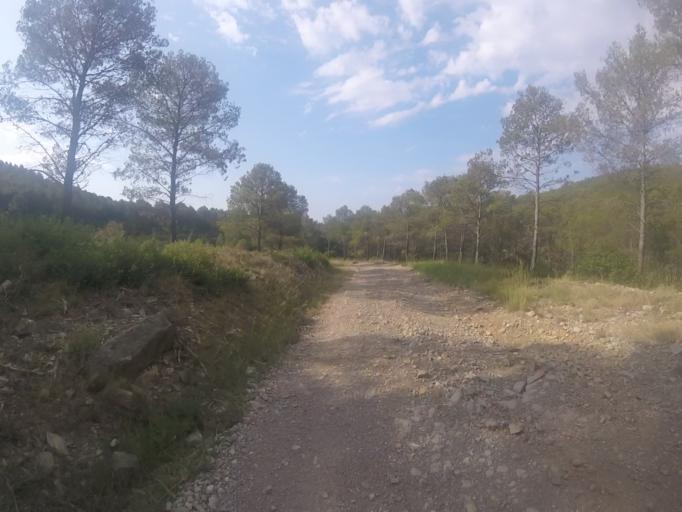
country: ES
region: Valencia
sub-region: Provincia de Castello
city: Cervera del Maestre
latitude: 40.3994
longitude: 0.2055
